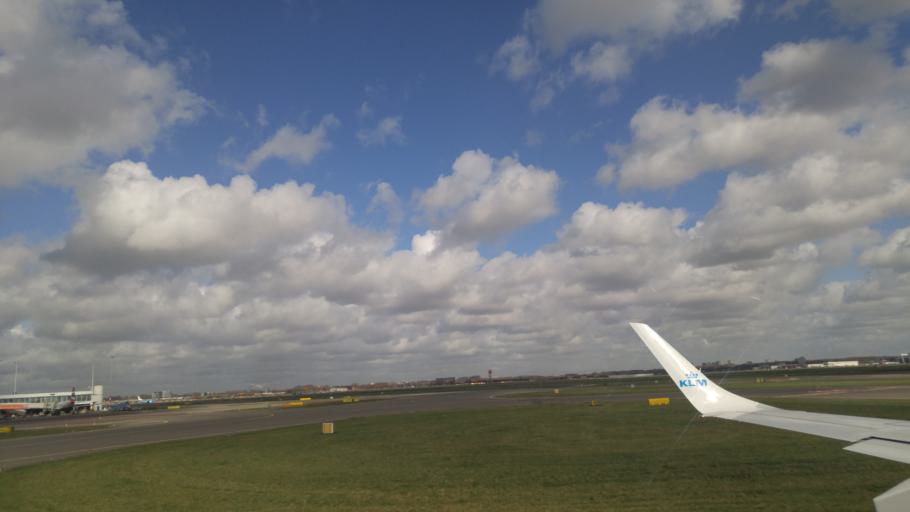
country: NL
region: North Holland
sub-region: Gemeente Aalsmeer
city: Aalsmeer
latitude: 52.3041
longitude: 4.7724
